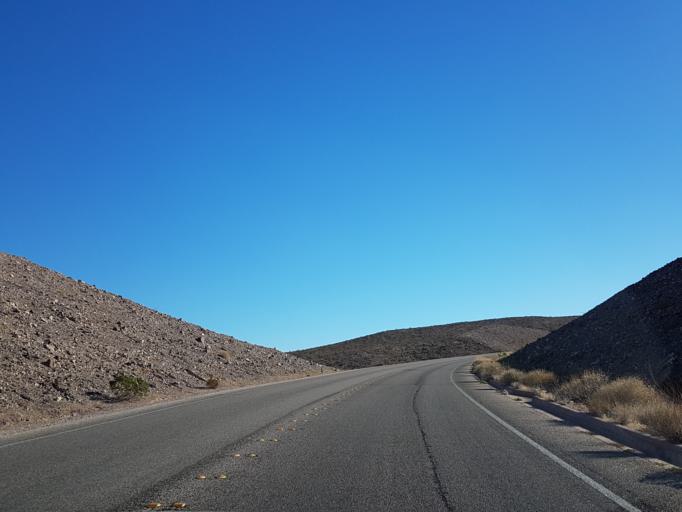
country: US
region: Nevada
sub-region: Clark County
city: Boulder City
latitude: 36.0924
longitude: -114.8255
